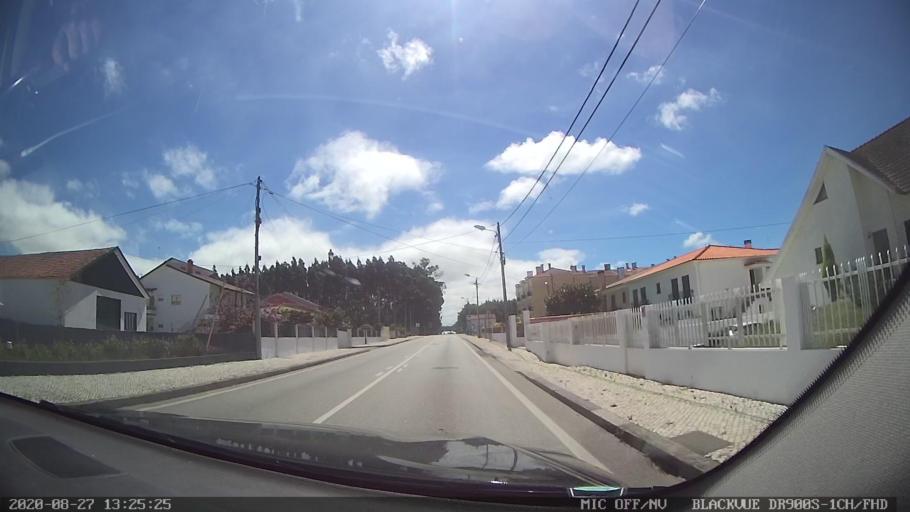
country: PT
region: Aveiro
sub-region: Vagos
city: Vagos
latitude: 40.5466
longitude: -8.6789
